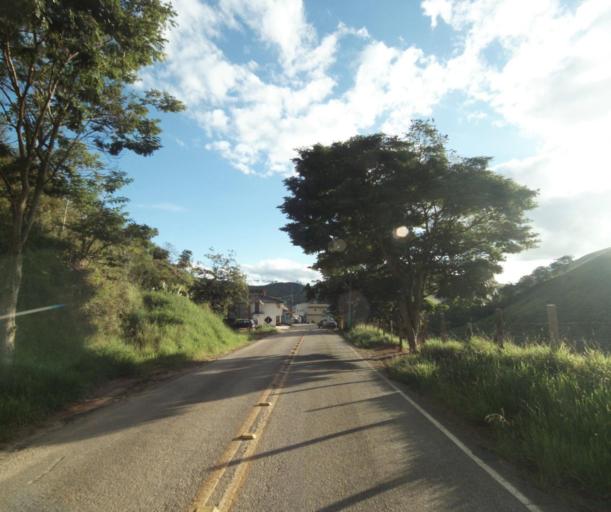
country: BR
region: Espirito Santo
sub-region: Guacui
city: Guacui
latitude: -20.6166
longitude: -41.6805
